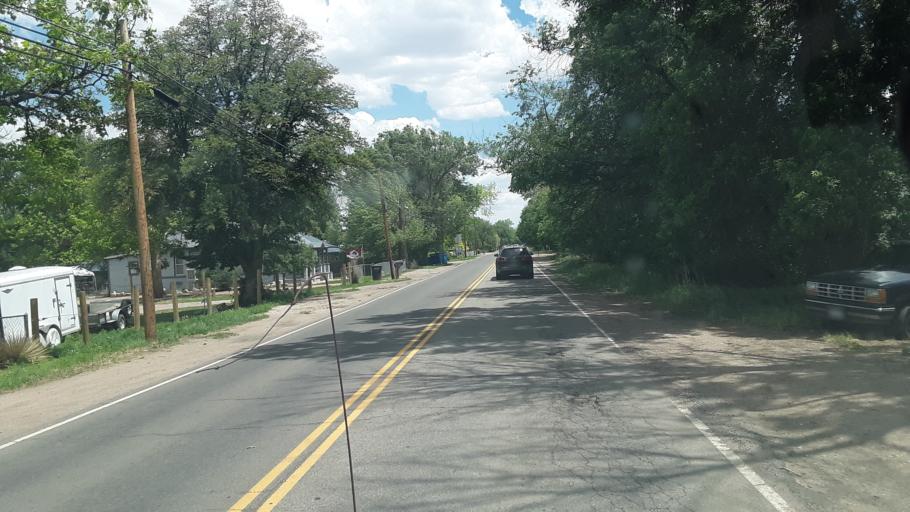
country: US
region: Colorado
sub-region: Fremont County
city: Florence
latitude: 38.3995
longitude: -105.1329
